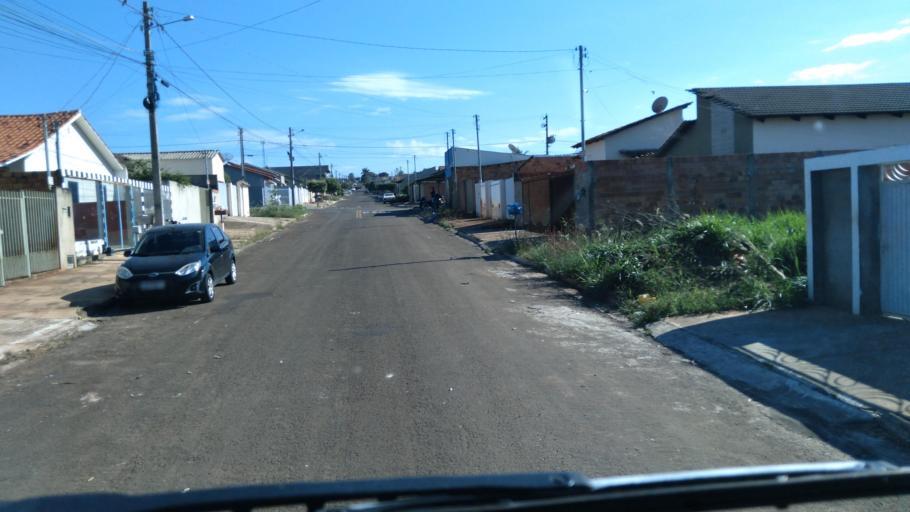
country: BR
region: Goias
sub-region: Mineiros
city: Mineiros
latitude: -17.5756
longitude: -52.5719
